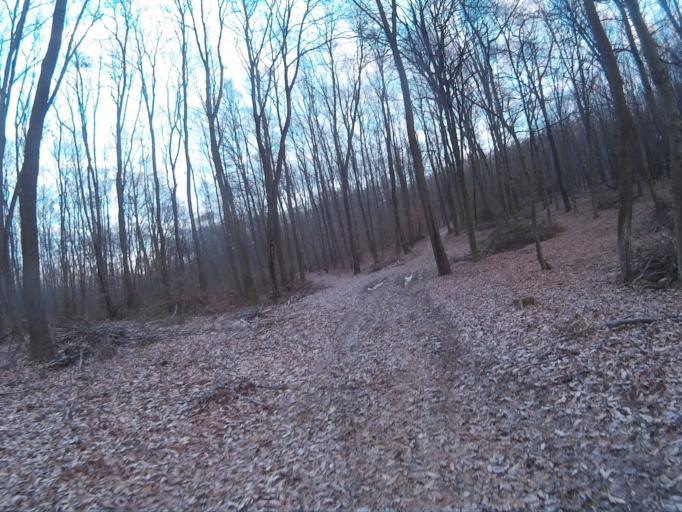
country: HU
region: Nograd
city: Rimoc
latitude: 48.0038
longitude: 19.4368
